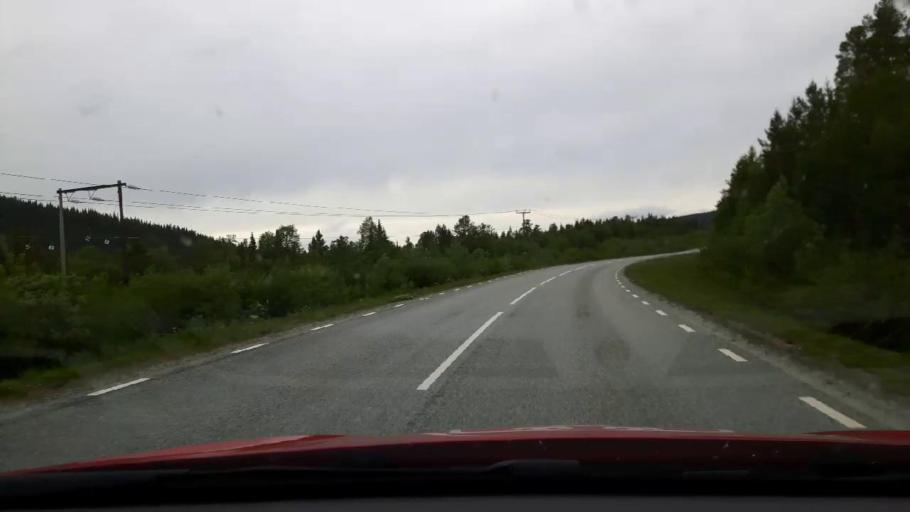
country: SE
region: Jaemtland
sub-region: Are Kommun
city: Are
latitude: 62.5707
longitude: 12.5608
